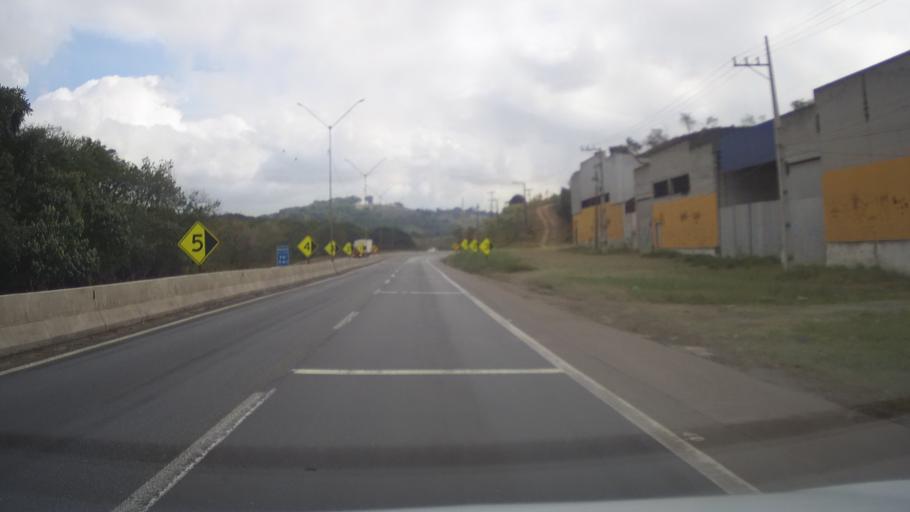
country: BR
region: Minas Gerais
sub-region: Extrema
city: Extrema
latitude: -22.8284
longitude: -46.3143
